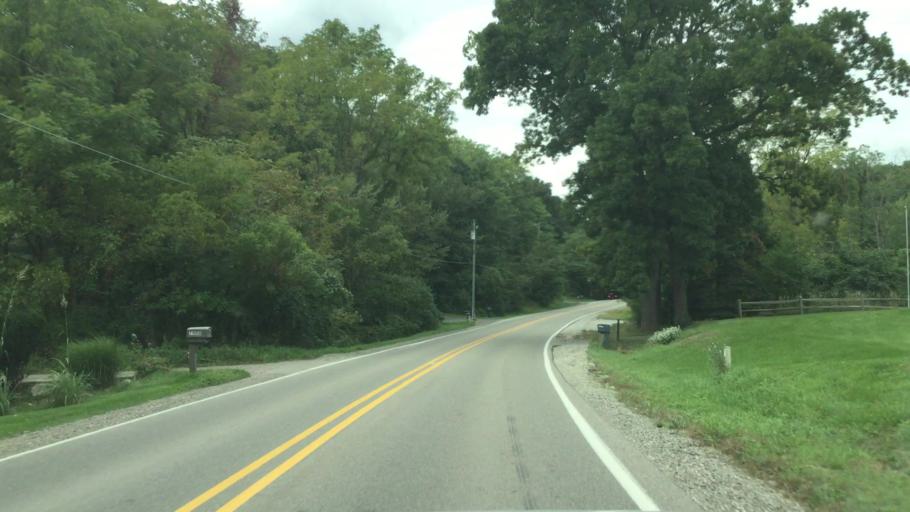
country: US
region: Michigan
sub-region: Livingston County
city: Whitmore Lake
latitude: 42.4623
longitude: -83.7906
